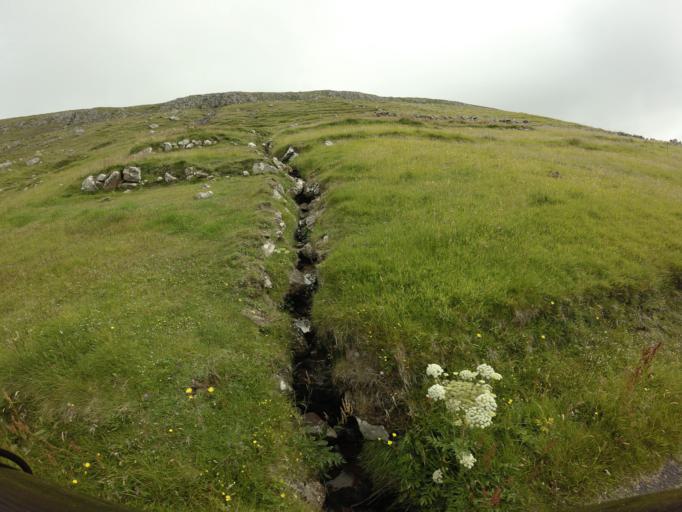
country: FO
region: Sandoy
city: Sandur
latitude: 61.7985
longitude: -6.7517
